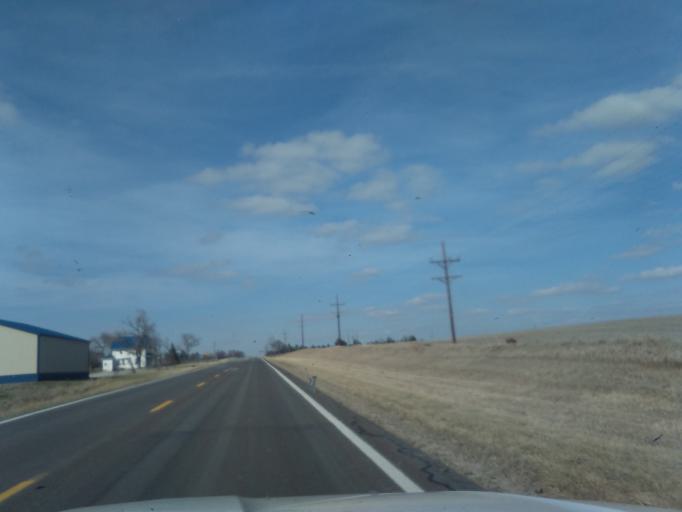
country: US
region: Nebraska
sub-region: Gage County
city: Beatrice
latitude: 40.1276
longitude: -96.9354
